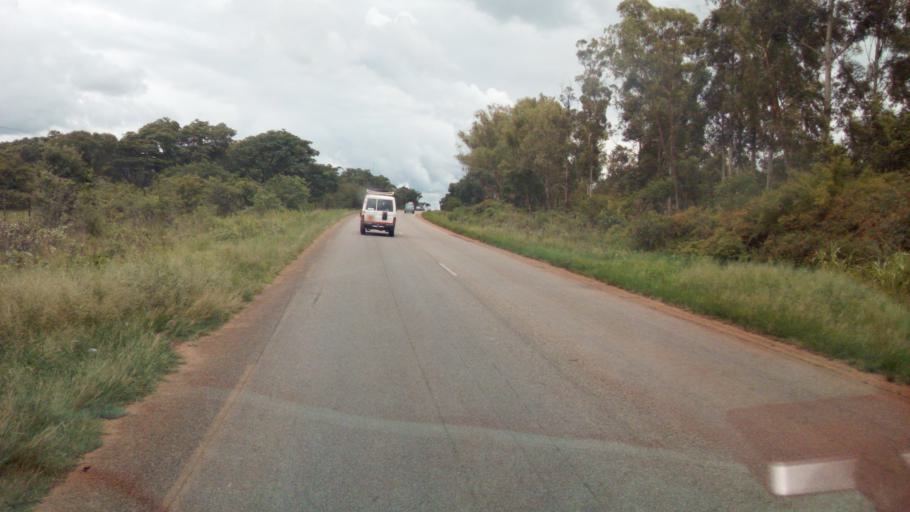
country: ZW
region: Harare
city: Harare
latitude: -17.7128
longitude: 31.0142
